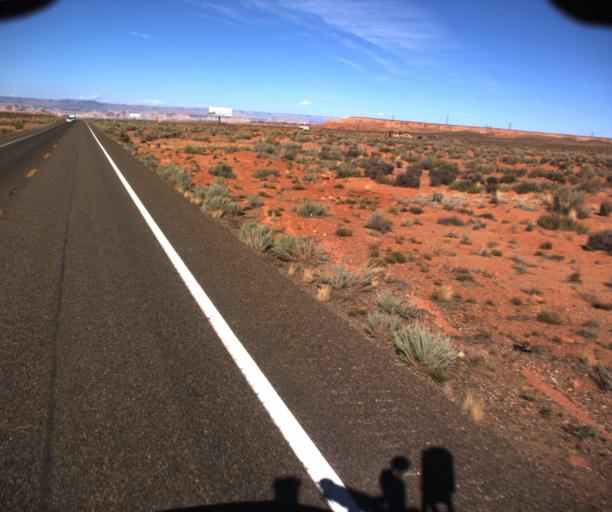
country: US
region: Arizona
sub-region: Coconino County
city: Page
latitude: 36.8639
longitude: -111.5044
